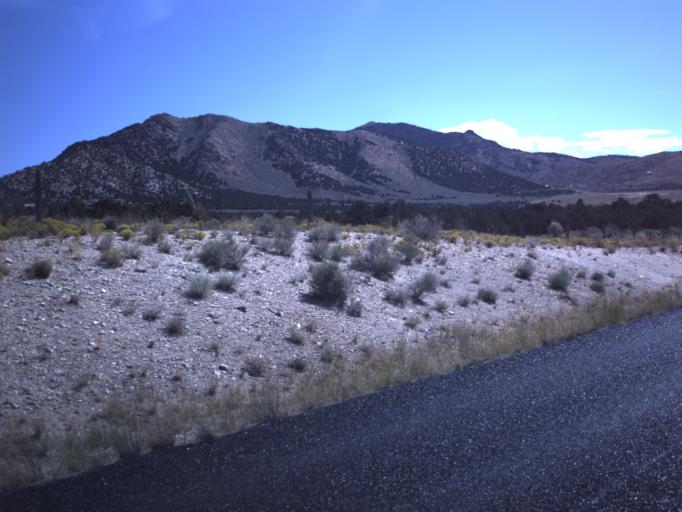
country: US
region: Utah
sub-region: Utah County
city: Genola
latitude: 39.9312
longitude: -112.1681
